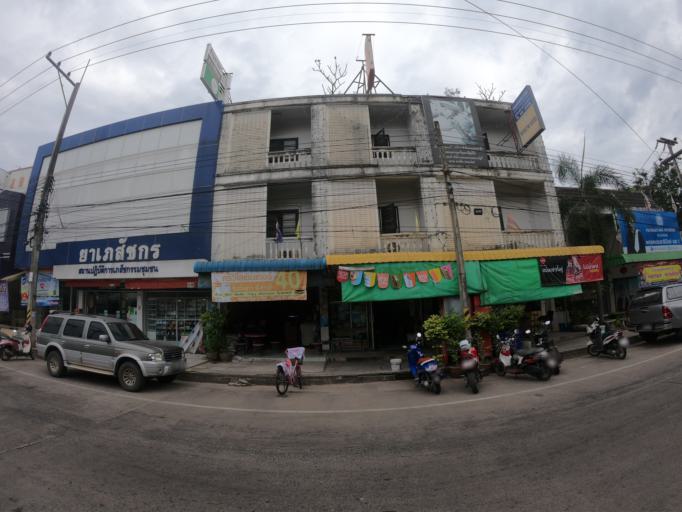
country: TH
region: Roi Et
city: Roi Et
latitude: 16.0547
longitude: 103.6569
